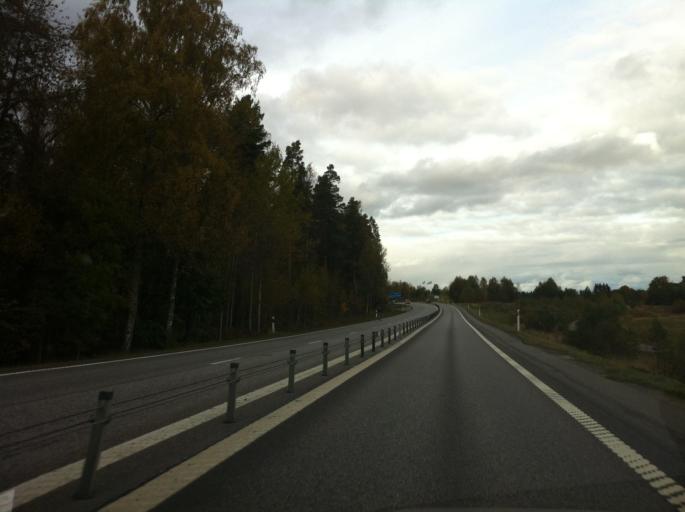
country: SE
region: OEstergoetland
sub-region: Motala Kommun
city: Motala
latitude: 58.6007
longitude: 14.9866
